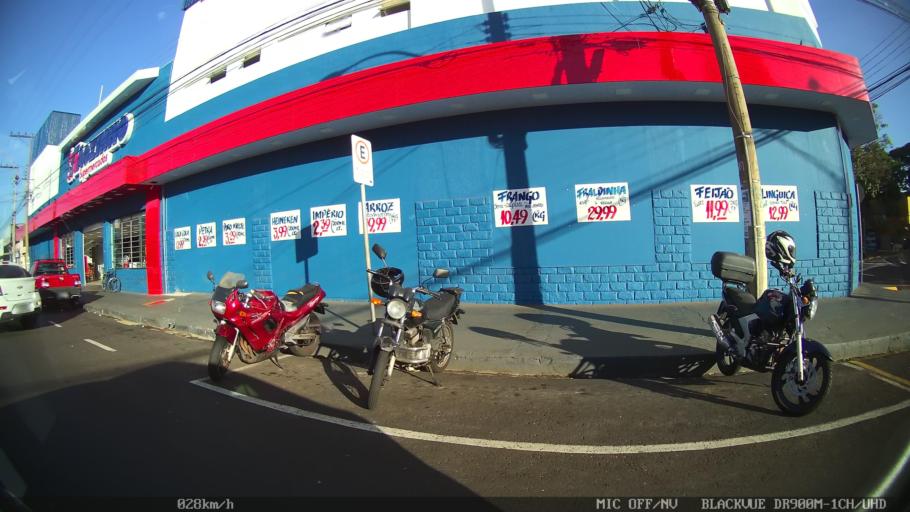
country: BR
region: Sao Paulo
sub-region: Franca
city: Franca
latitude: -20.5273
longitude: -47.3895
